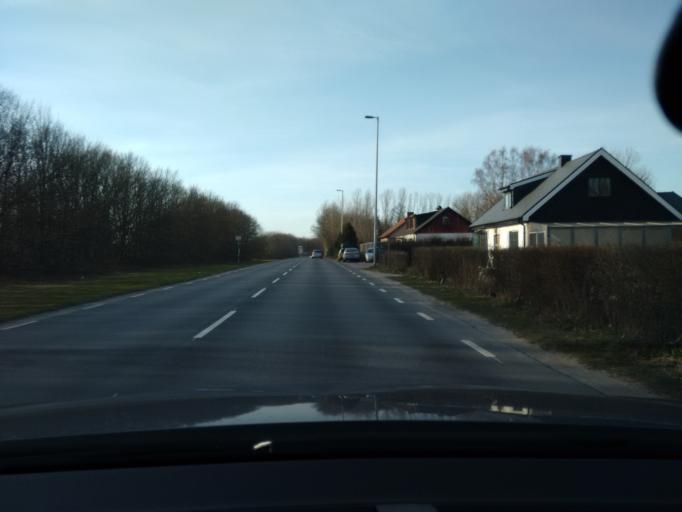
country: SE
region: Skane
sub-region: Lunds Kommun
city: Lund
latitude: 55.7259
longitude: 13.1812
